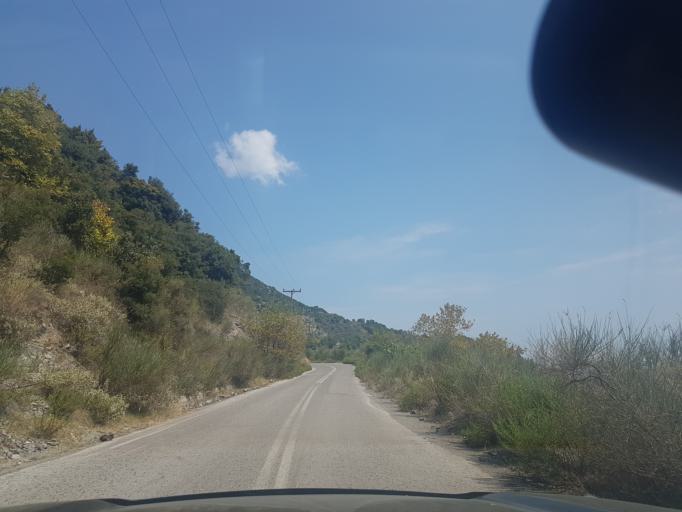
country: GR
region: Central Greece
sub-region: Nomos Evvoias
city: Yimnon
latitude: 38.6348
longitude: 23.8902
